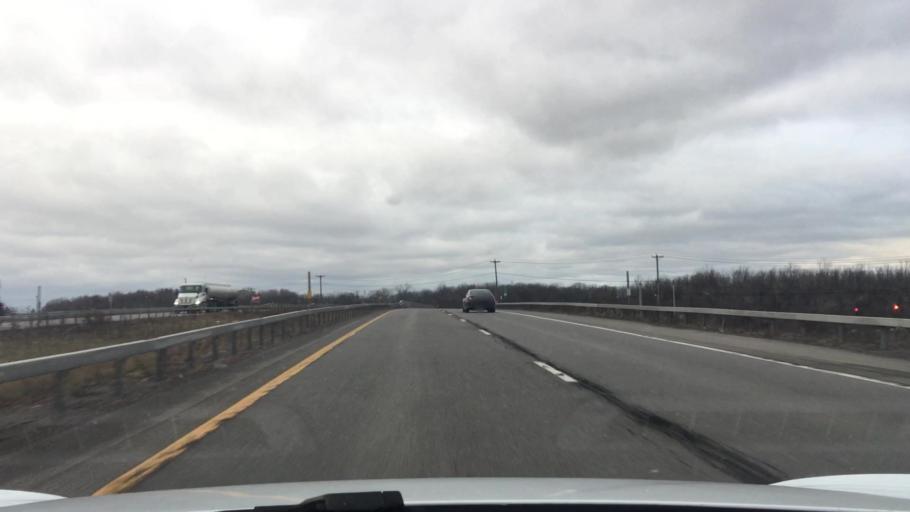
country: US
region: New York
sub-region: Niagara County
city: Niagara Falls
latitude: 43.1075
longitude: -78.9906
